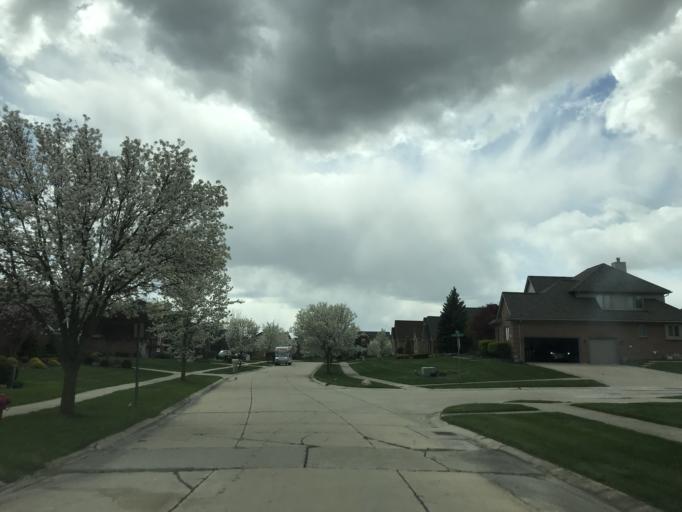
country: US
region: Michigan
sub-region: Wayne County
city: Plymouth
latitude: 42.3799
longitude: -83.5242
